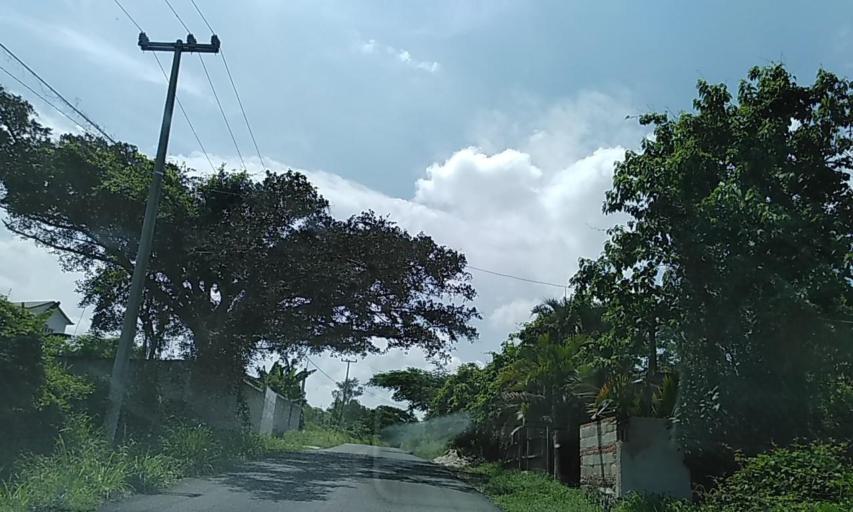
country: MX
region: Veracruz
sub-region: Emiliano Zapata
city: Dos Rios
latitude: 19.4382
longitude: -96.7791
